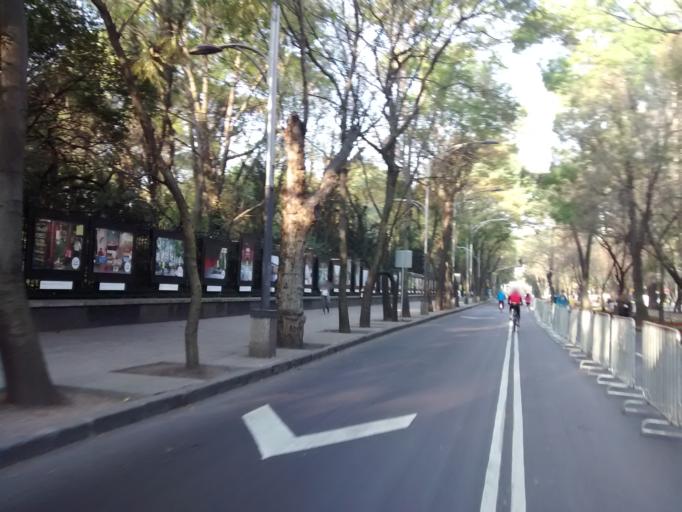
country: MX
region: Mexico City
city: Polanco
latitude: 19.4252
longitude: -99.1889
